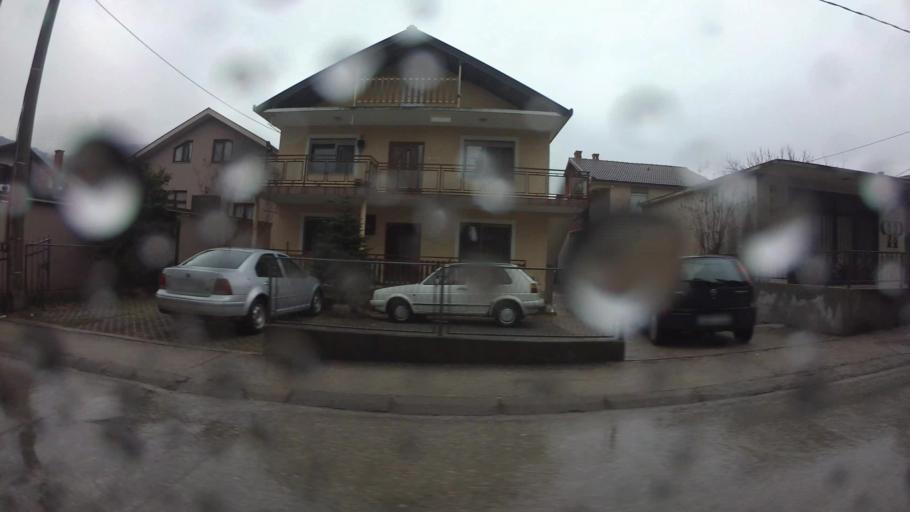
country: BA
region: Federation of Bosnia and Herzegovina
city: Cim
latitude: 43.3482
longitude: 17.7865
